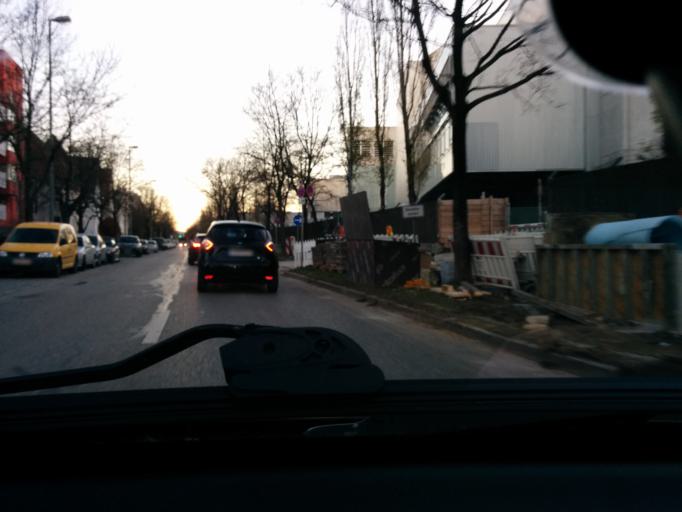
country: DE
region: Bavaria
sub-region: Upper Bavaria
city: Munich
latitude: 48.1809
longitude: 11.5633
